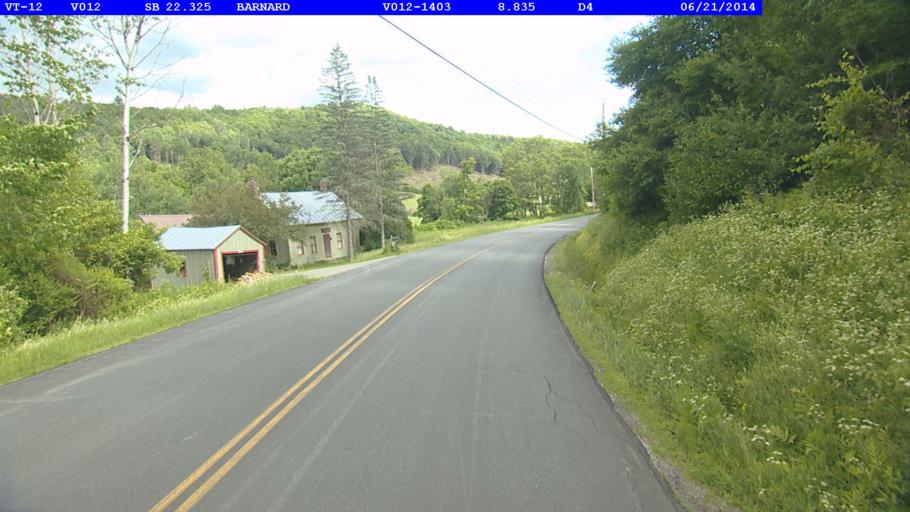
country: US
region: Vermont
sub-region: Orange County
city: Randolph
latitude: 43.7827
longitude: -72.6378
